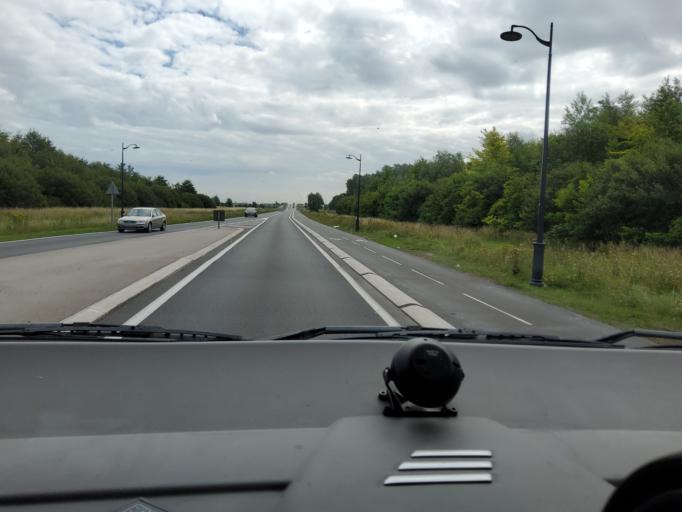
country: FR
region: Nord-Pas-de-Calais
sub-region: Departement du Nord
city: Gravelines
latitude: 50.9960
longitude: 2.1570
